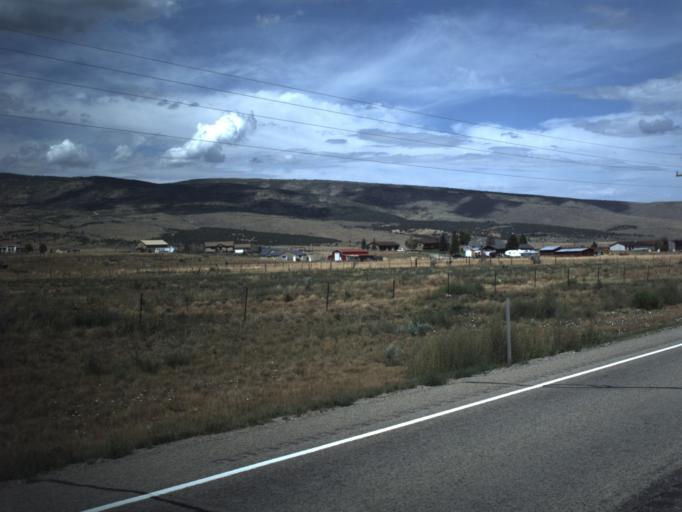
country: US
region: Utah
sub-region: Sanpete County
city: Fairview
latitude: 39.7713
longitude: -111.4876
